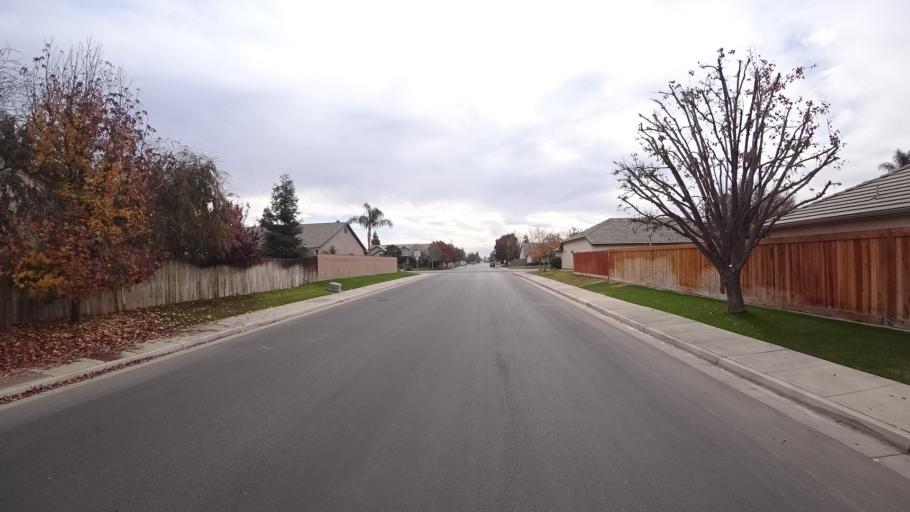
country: US
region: California
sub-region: Kern County
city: Rosedale
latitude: 35.4225
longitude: -119.1303
